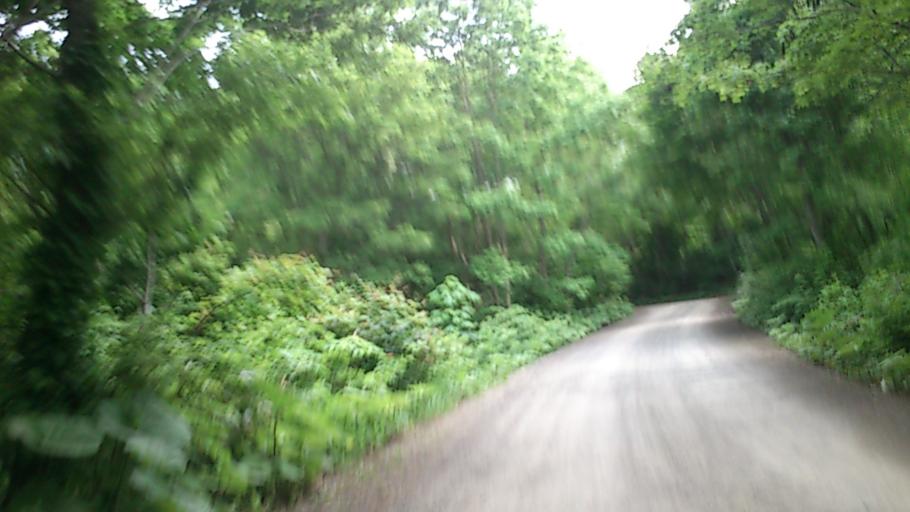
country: JP
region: Aomori
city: Hirosaki
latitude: 40.5620
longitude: 140.1793
